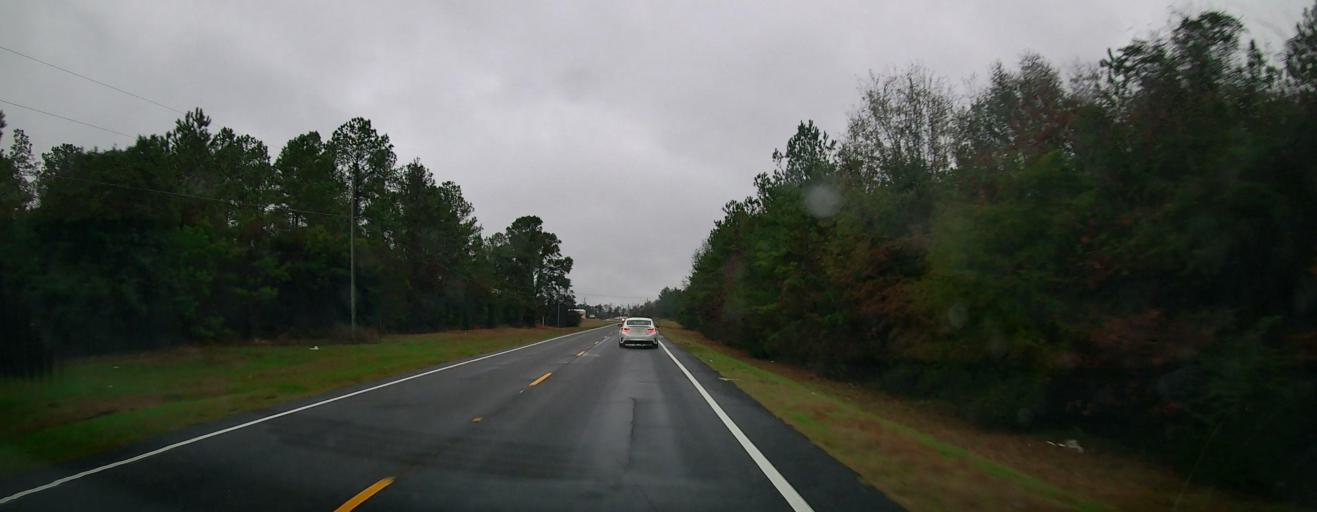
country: US
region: Alabama
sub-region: Chilton County
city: Clanton
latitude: 32.6807
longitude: -86.7907
